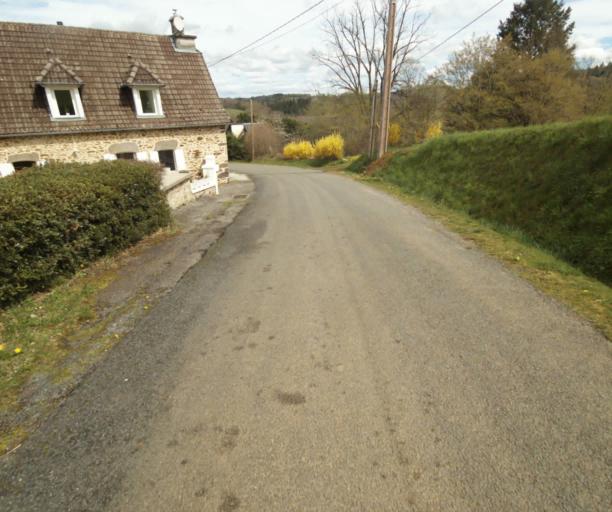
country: FR
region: Limousin
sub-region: Departement de la Correze
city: Laguenne
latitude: 45.2308
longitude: 1.8503
